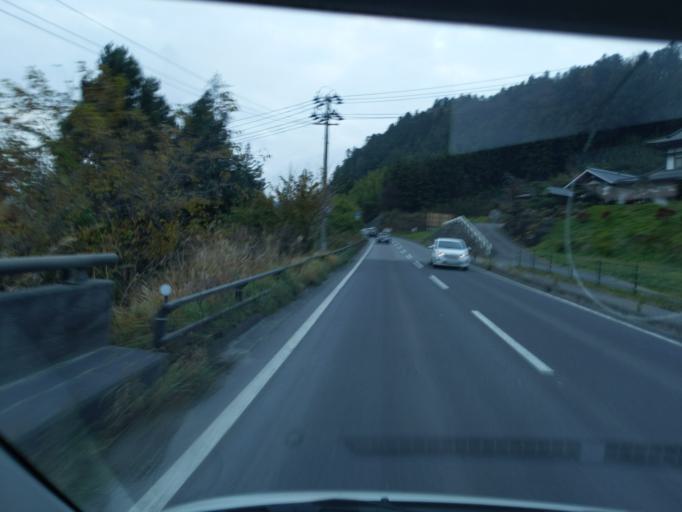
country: JP
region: Iwate
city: Ichinoseki
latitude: 38.9871
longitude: 141.2480
